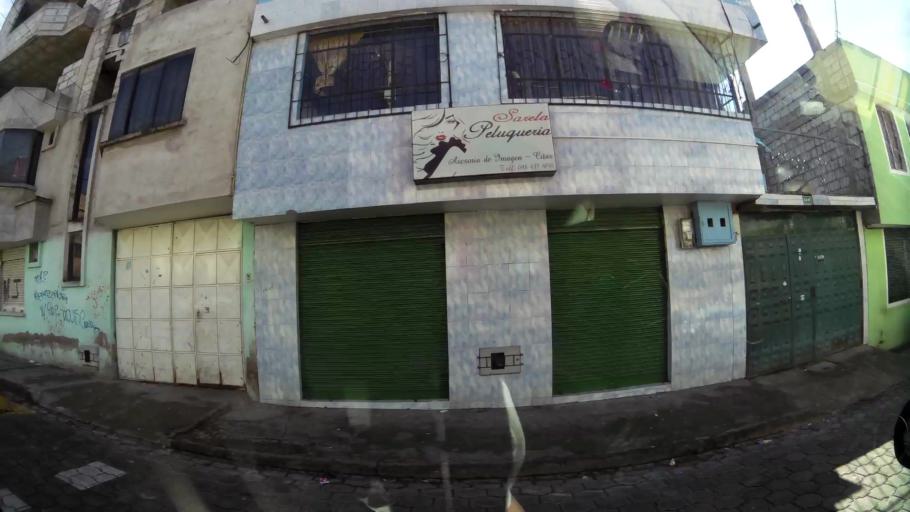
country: EC
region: Pichincha
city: Quito
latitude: -0.2991
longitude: -78.5661
